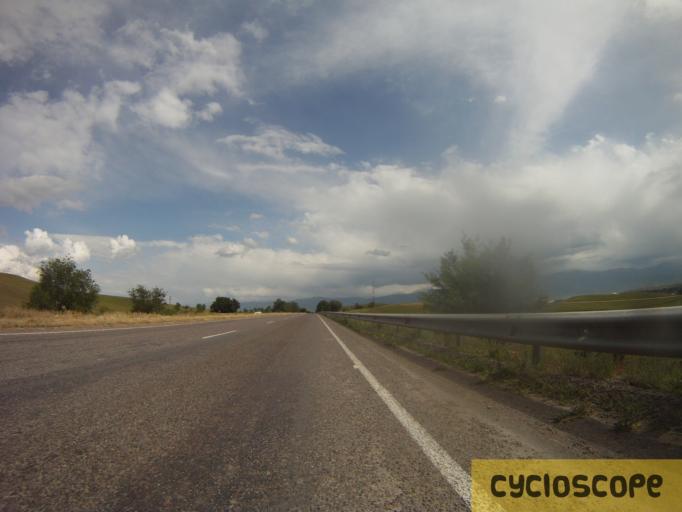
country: KZ
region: Almaty Oblysy
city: Burunday
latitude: 43.2482
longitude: 76.3255
